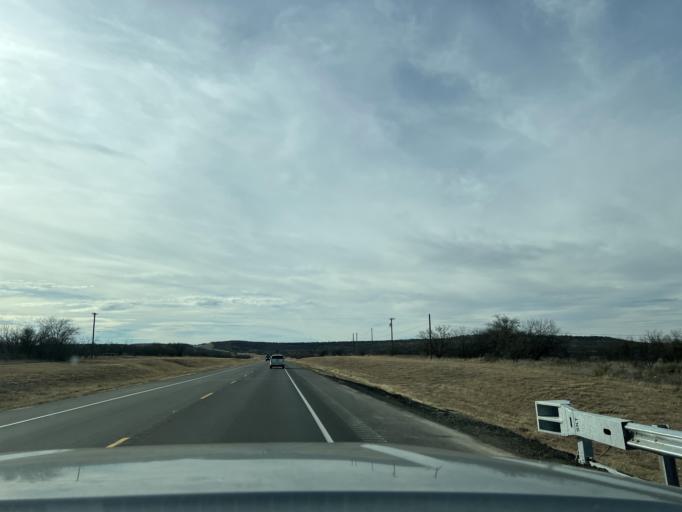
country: US
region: Texas
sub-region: Shackelford County
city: Albany
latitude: 32.7130
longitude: -99.3507
